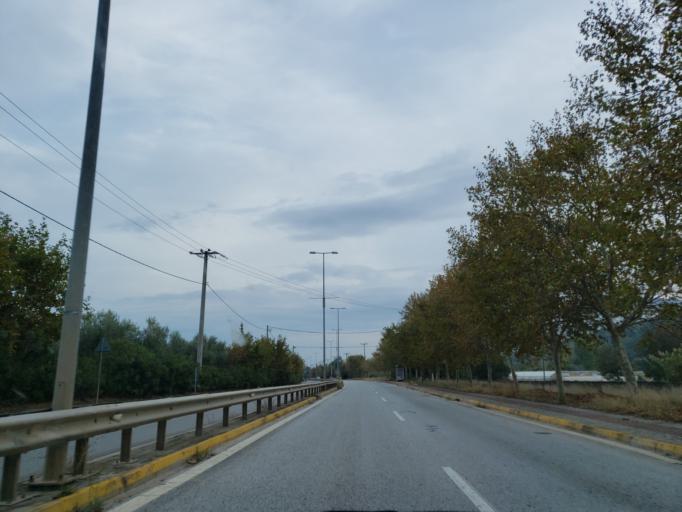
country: GR
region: Attica
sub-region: Nomarchia Anatolikis Attikis
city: Marathonas
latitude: 38.1400
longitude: 23.9662
